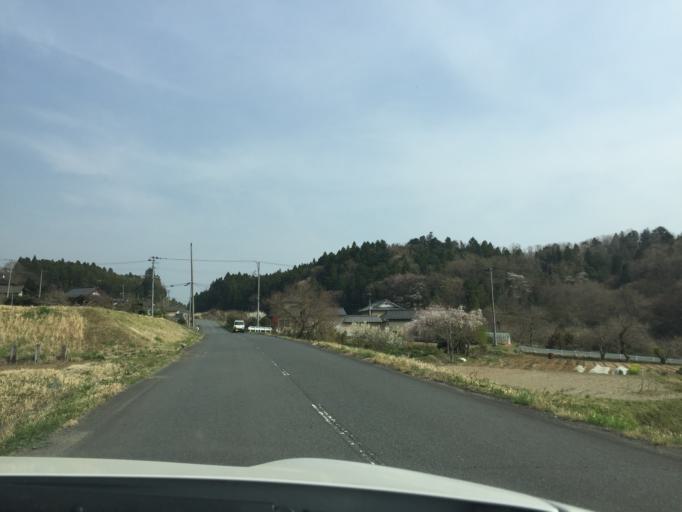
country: JP
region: Fukushima
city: Iwaki
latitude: 37.0262
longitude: 140.7583
